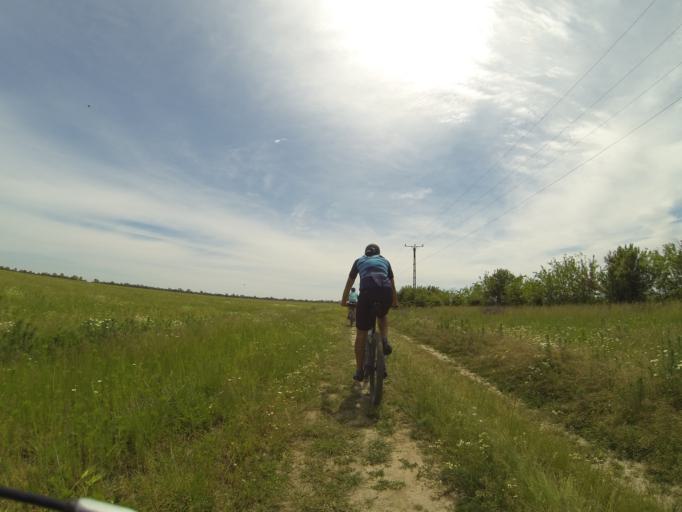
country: RO
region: Dolj
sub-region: Comuna Leu
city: Leu
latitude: 44.2036
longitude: 23.9679
